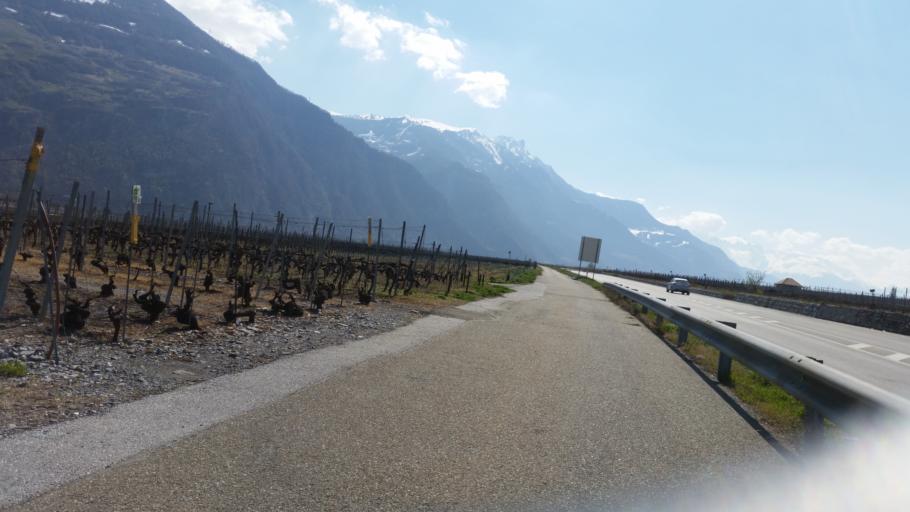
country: CH
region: Valais
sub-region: Conthey District
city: Ardon
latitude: 46.2049
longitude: 7.2504
